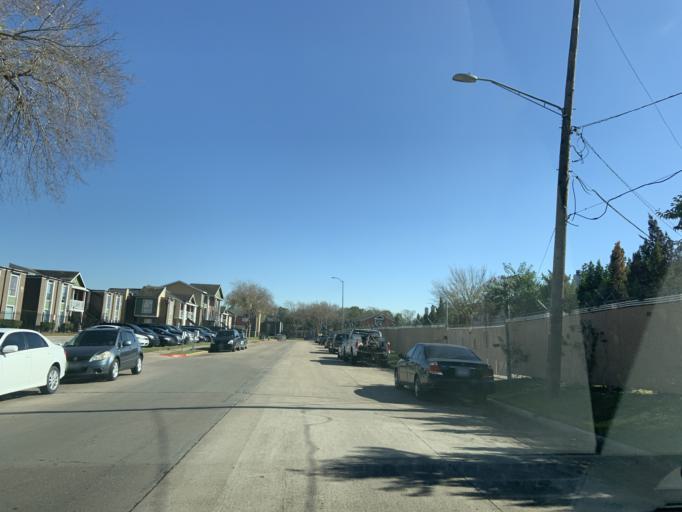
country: US
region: Texas
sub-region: Harris County
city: Bellaire
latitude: 29.6787
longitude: -95.5076
